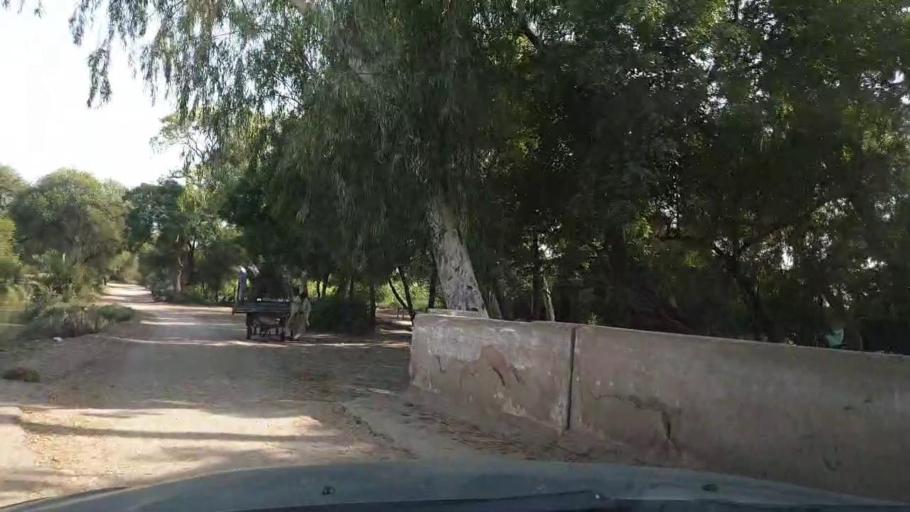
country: PK
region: Sindh
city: Bulri
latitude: 24.9055
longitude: 68.3746
